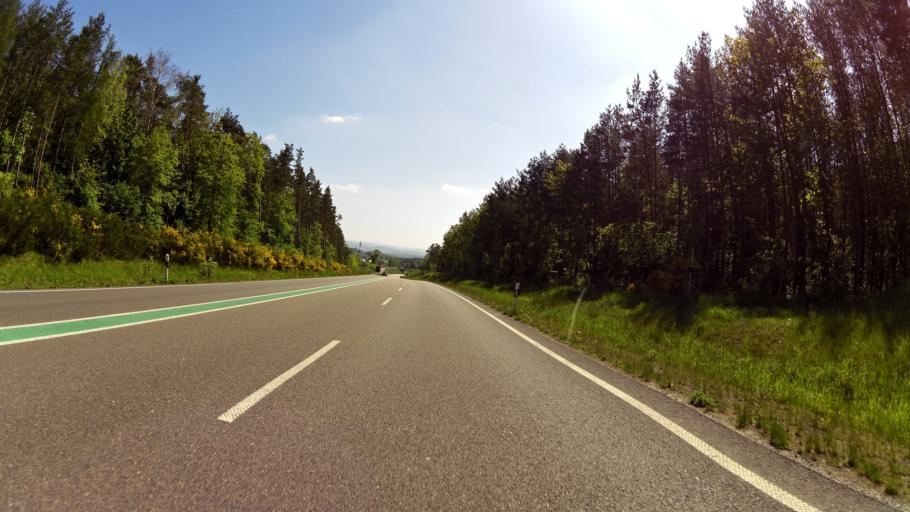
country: DE
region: Saxony
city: Pirna
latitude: 50.9969
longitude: 13.9387
